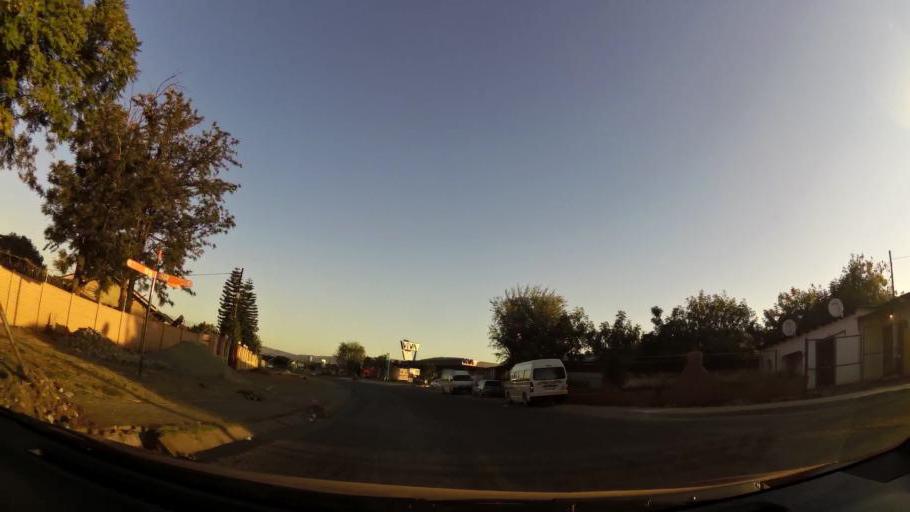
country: ZA
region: North-West
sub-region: Bojanala Platinum District Municipality
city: Rustenburg
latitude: -25.6399
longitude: 27.2091
